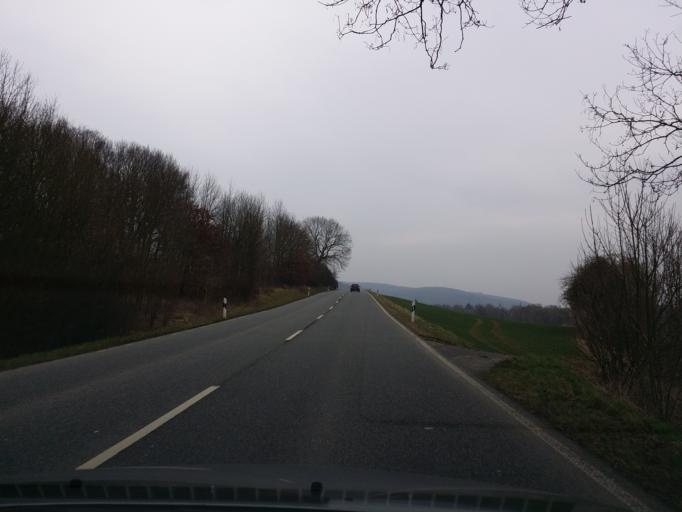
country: DE
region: Hesse
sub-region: Regierungsbezirk Darmstadt
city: Waldems
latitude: 50.2596
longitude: 8.3027
